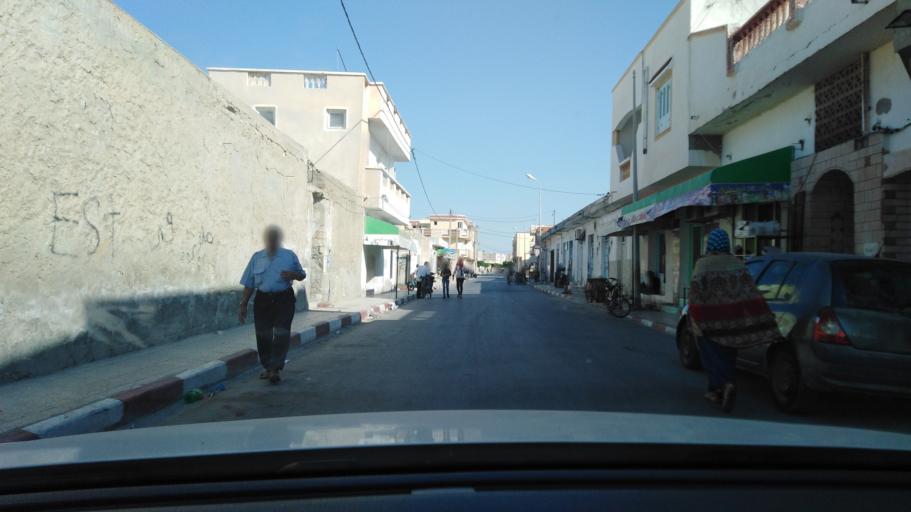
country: TN
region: Qabis
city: Gabes
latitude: 33.9386
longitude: 10.0674
